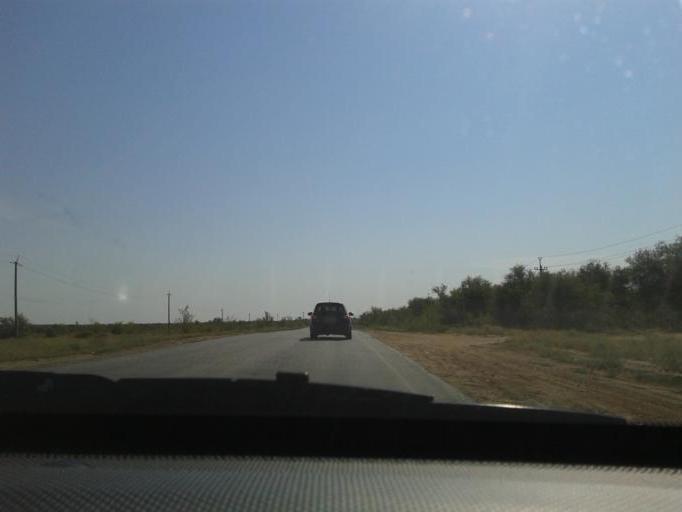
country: RU
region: Volgograd
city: Leninsk
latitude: 48.6967
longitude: 45.2710
